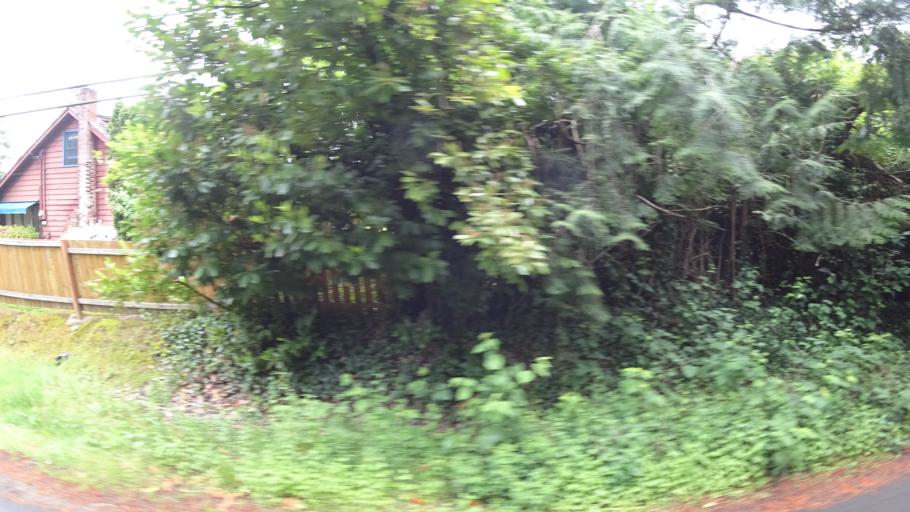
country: US
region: Oregon
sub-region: Washington County
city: Garden Home-Whitford
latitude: 45.4648
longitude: -122.7658
